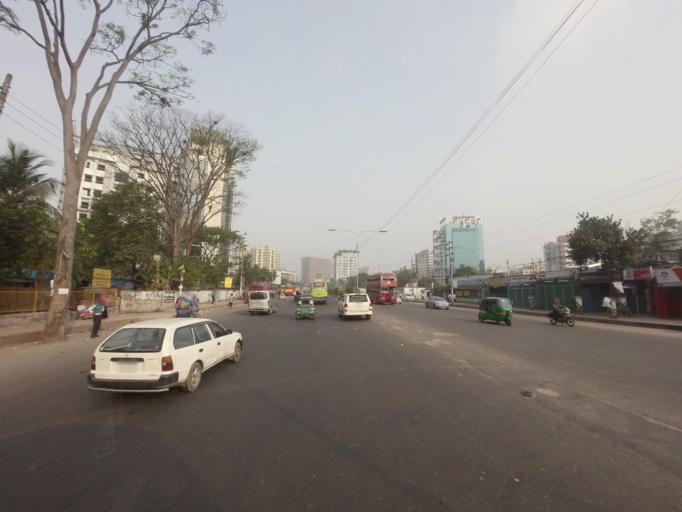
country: BD
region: Dhaka
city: Azimpur
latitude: 23.7762
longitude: 90.3638
